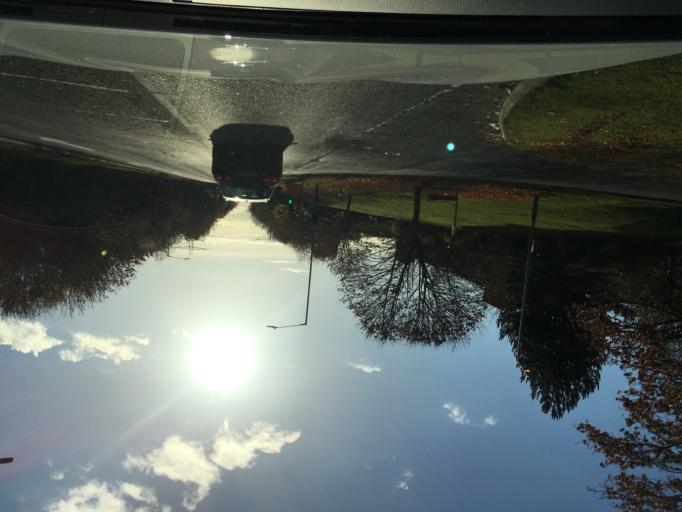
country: GB
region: England
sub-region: Warwickshire
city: Royal Leamington Spa
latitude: 52.2784
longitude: -1.5517
